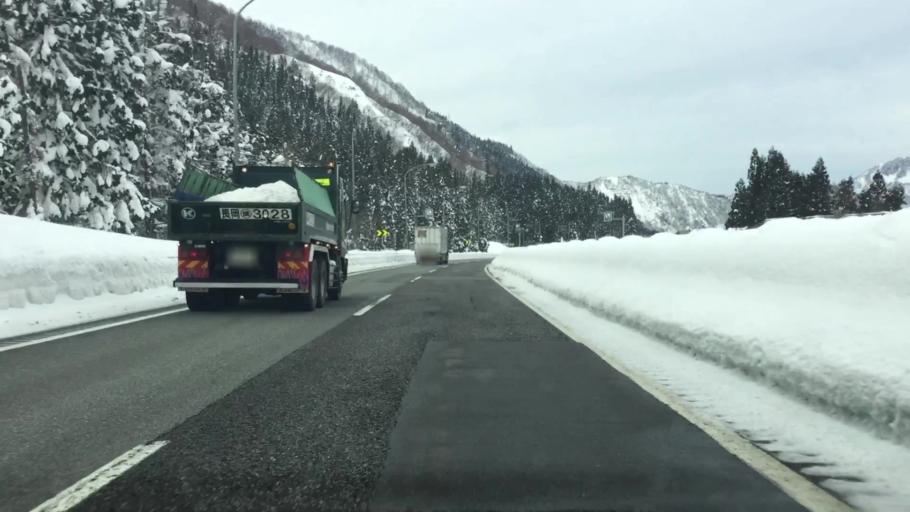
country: JP
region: Niigata
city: Shiozawa
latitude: 36.8862
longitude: 138.8502
